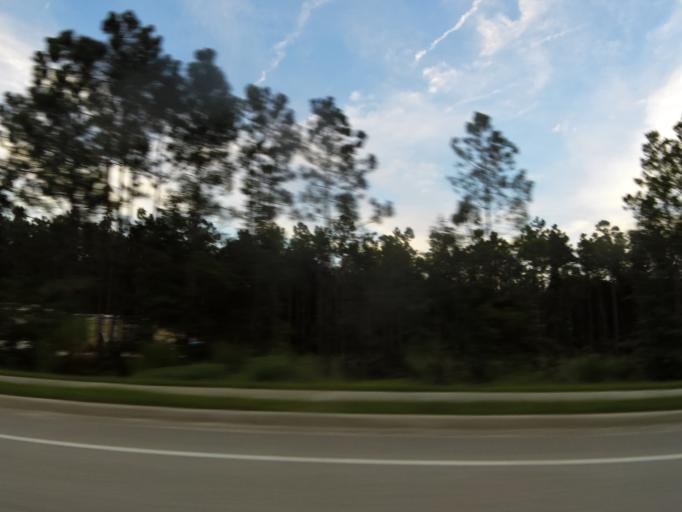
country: US
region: Florida
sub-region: Saint Johns County
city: Fruit Cove
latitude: 30.0894
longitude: -81.5807
